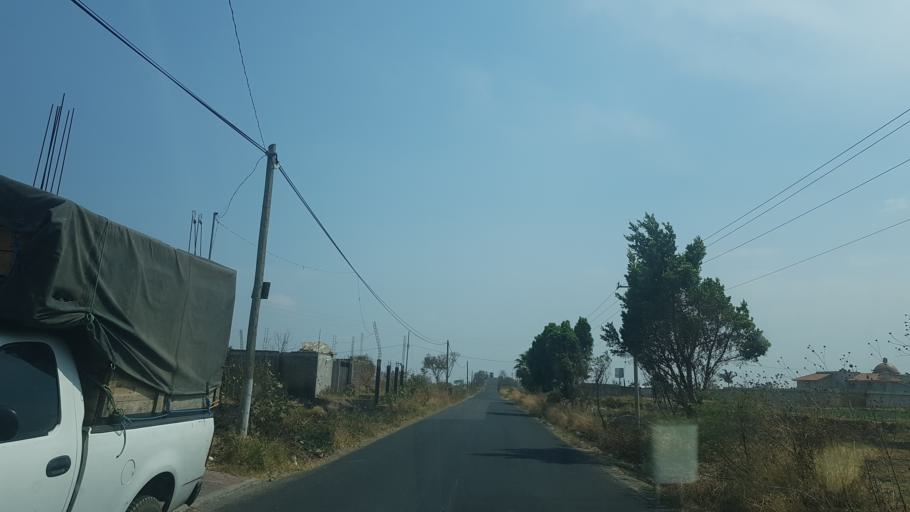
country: MX
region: Puebla
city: San Juan Tianguismanalco
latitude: 18.9393
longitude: -98.4541
